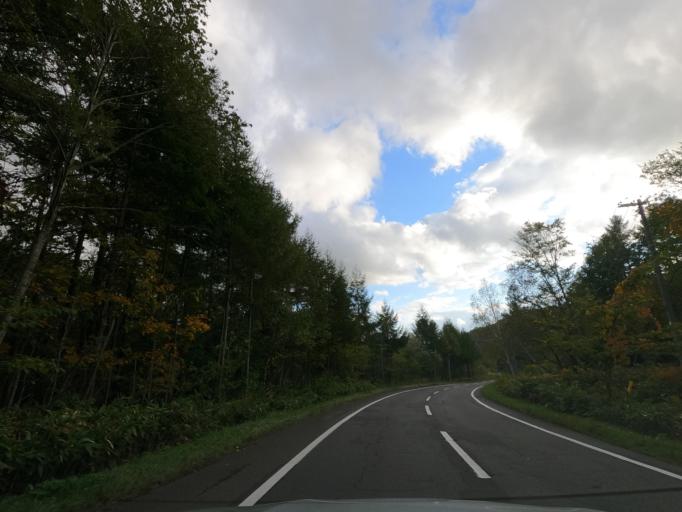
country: JP
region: Hokkaido
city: Date
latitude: 42.6634
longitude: 141.0727
